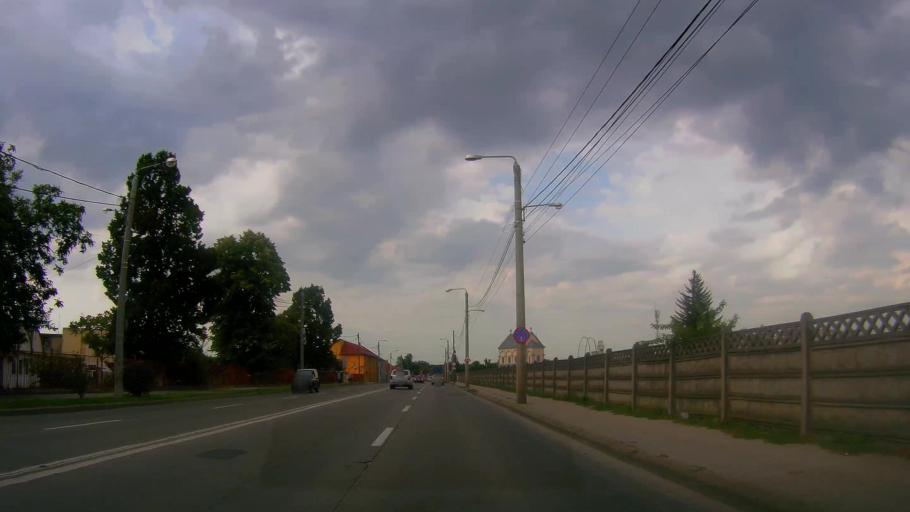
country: RO
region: Satu Mare
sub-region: Municipiul Satu Mare
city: Satu Mare
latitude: 47.7931
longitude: 22.8930
